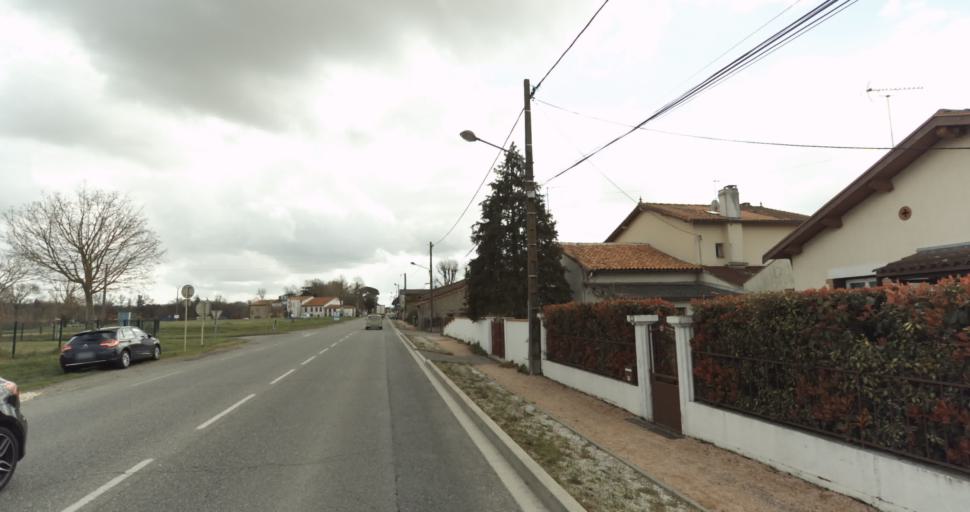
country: FR
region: Midi-Pyrenees
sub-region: Departement de la Haute-Garonne
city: Auterive
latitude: 43.3459
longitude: 1.4739
